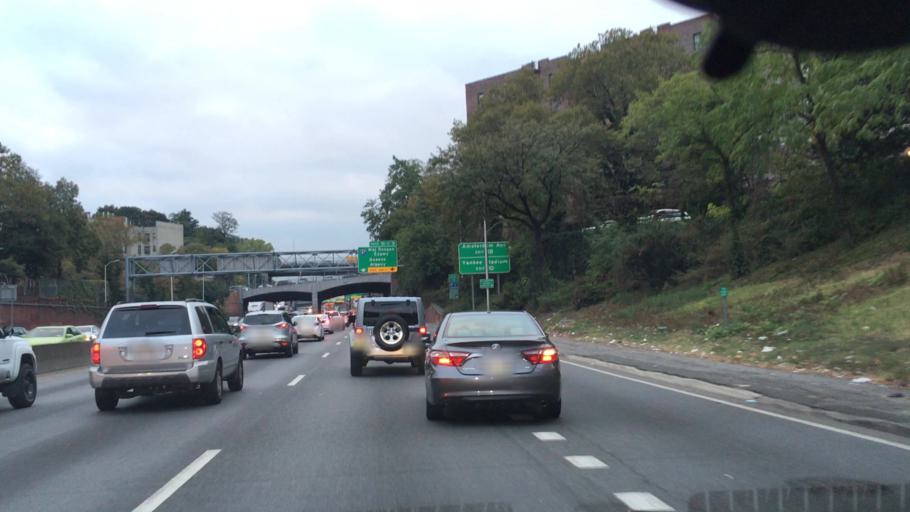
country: US
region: New York
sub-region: New York County
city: Inwood
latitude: 40.8453
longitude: -73.9146
